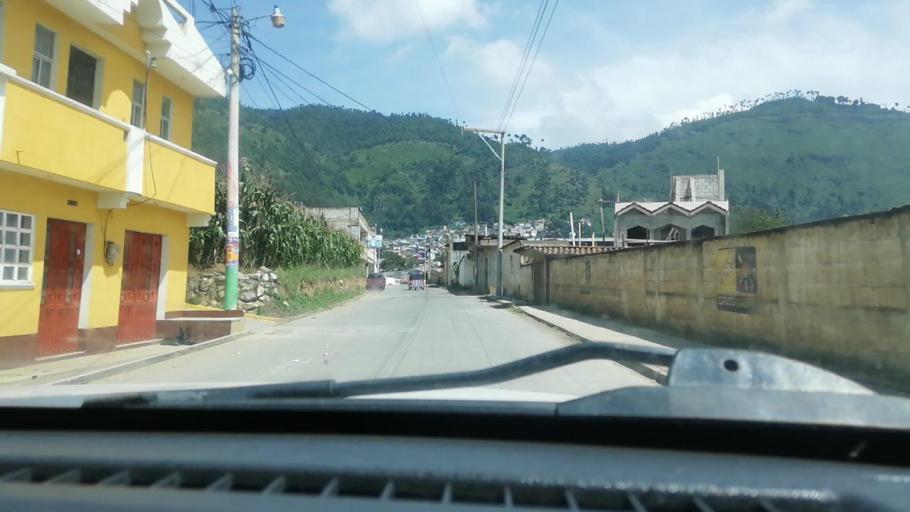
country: GT
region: Totonicapan
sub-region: Municipio de San Andres Xecul
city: San Andres Xecul
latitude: 14.9003
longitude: -91.4805
